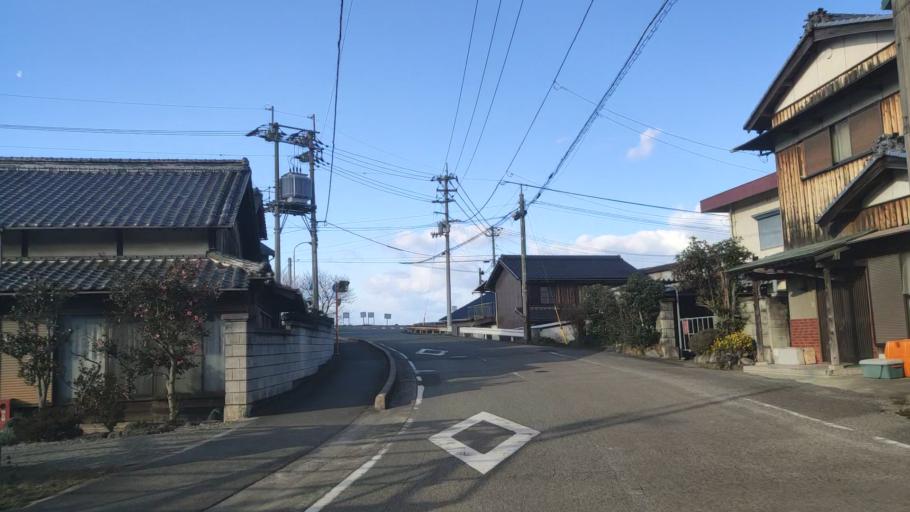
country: JP
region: Ehime
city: Saijo
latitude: 33.9066
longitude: 133.1292
